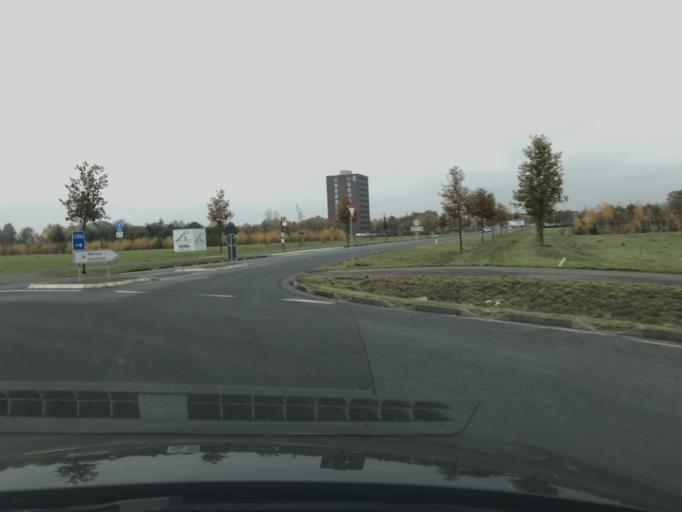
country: DE
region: North Rhine-Westphalia
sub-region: Regierungsbezirk Munster
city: Ladbergen
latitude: 52.1261
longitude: 7.6932
